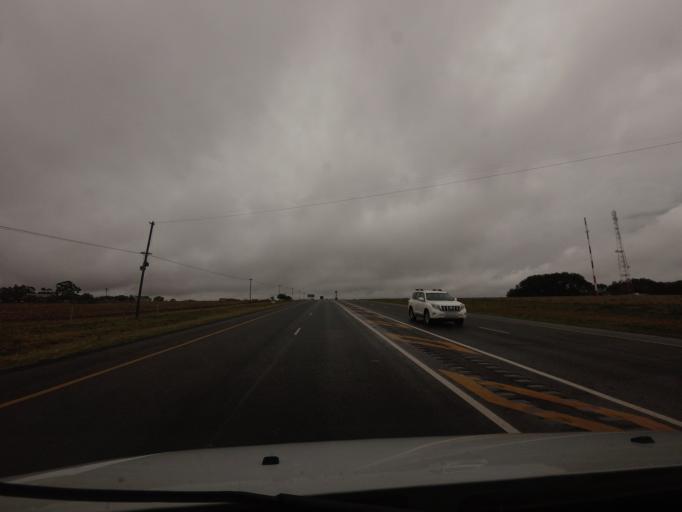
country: ZA
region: Mpumalanga
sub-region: Nkangala District Municipality
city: Belfast
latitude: -25.7712
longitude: 29.9512
